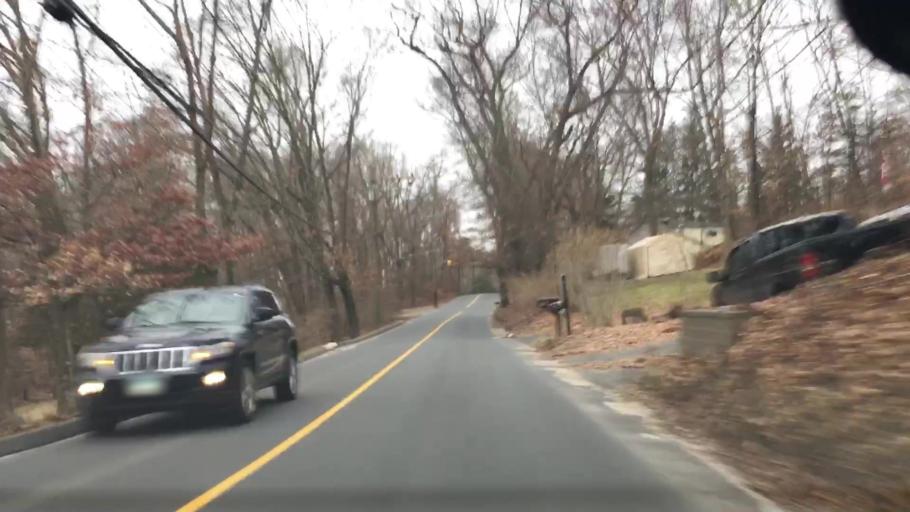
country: US
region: Connecticut
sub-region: Fairfield County
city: Bethel
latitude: 41.3936
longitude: -73.3998
